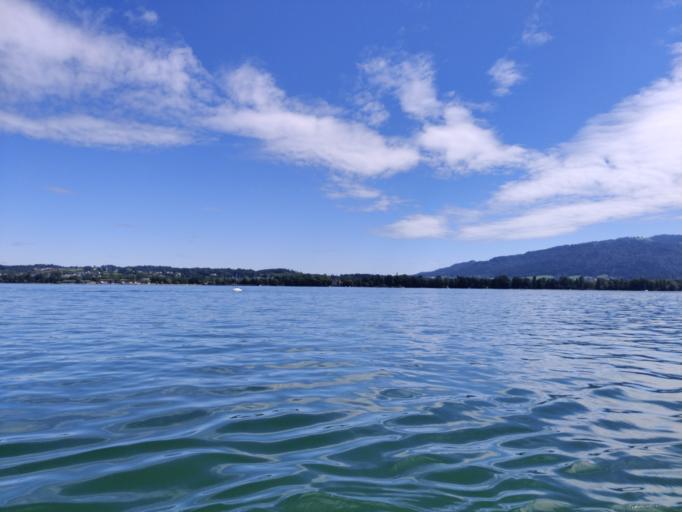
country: DE
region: Bavaria
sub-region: Swabia
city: Lindau
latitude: 47.5343
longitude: 9.7098
